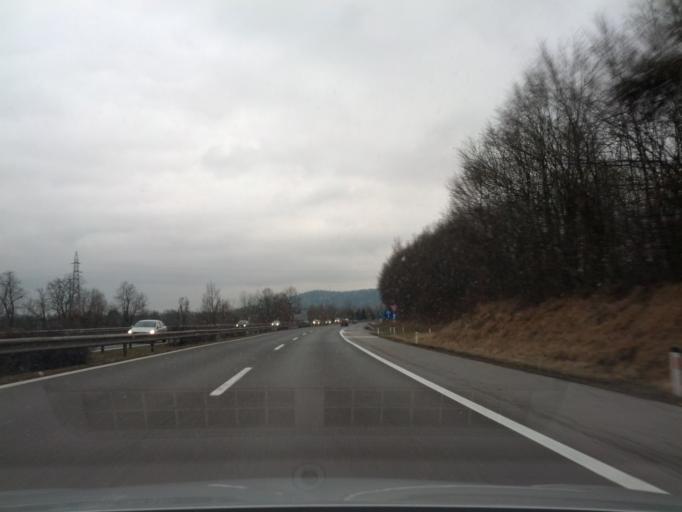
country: SI
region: Medvode
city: Zgornje Pirnice
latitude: 46.1229
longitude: 14.4810
